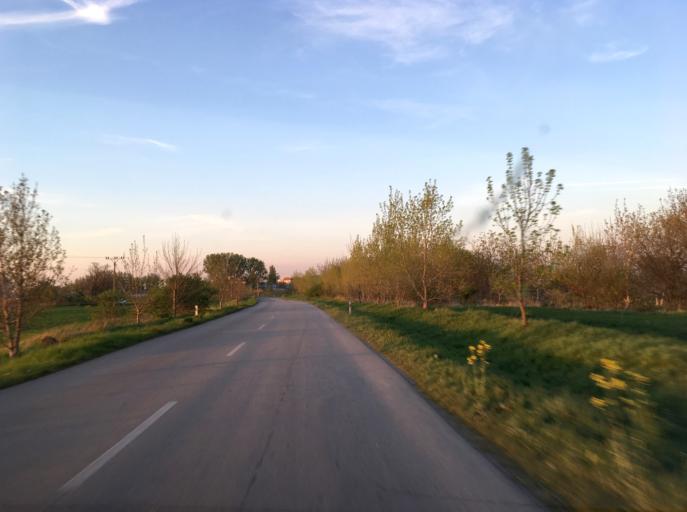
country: SK
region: Nitriansky
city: Kolarovo
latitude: 47.9015
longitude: 17.9726
